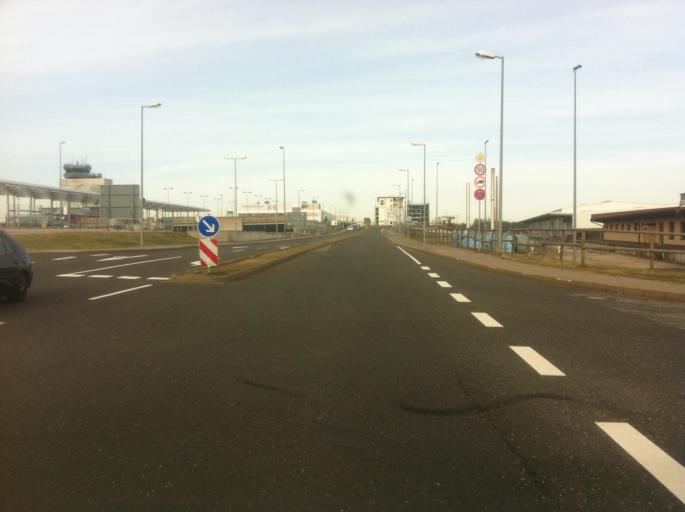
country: DE
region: Rheinland-Pfalz
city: Lautzenhausen
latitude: 49.9427
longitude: 7.2670
